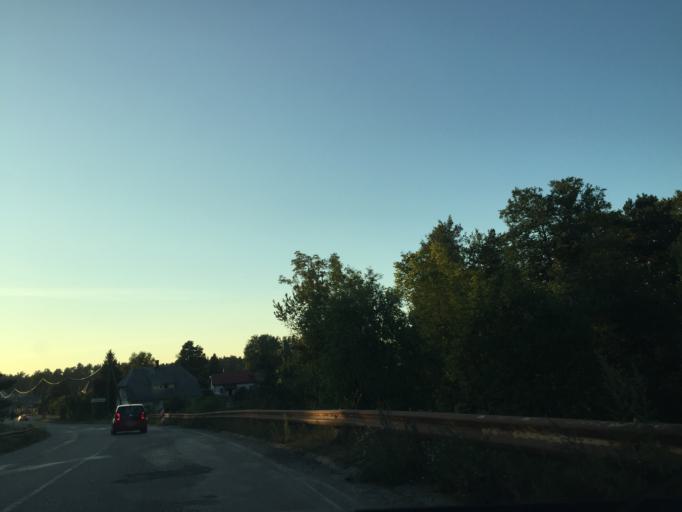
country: LV
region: Garkalne
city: Garkalne
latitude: 57.0411
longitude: 24.4137
